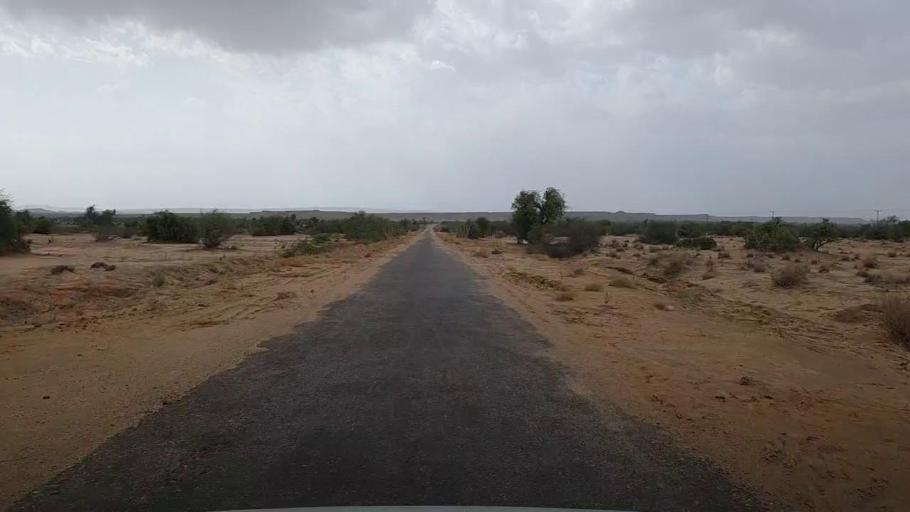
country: PK
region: Sindh
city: Jamshoro
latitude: 25.4037
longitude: 67.7084
